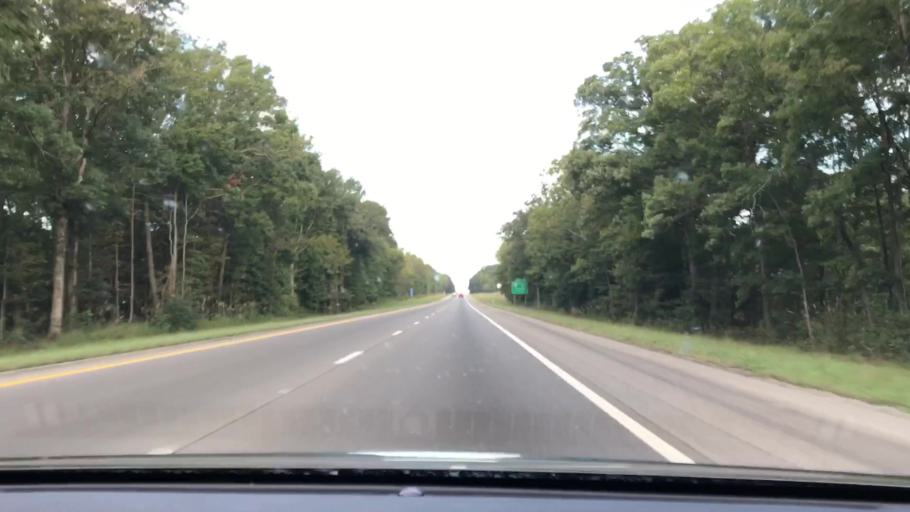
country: US
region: Tennessee
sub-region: Cheatham County
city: Pleasant View
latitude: 36.4374
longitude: -87.0796
